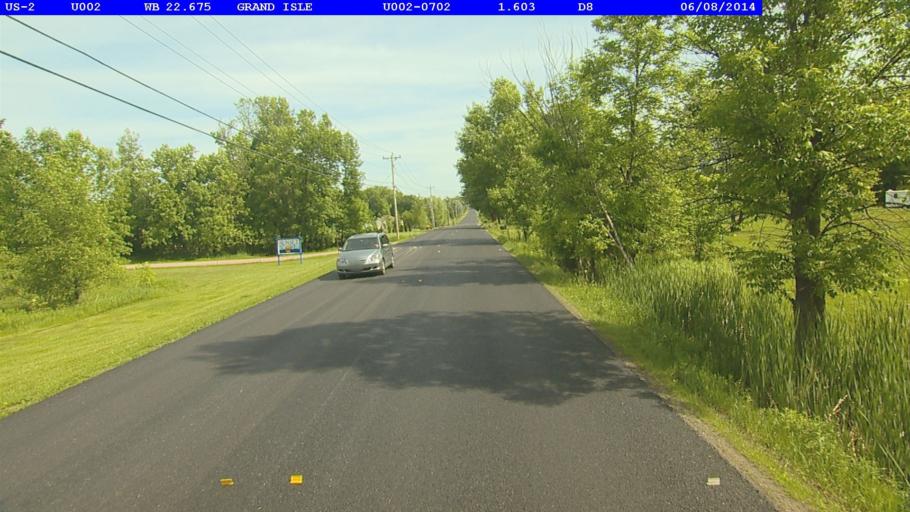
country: US
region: Vermont
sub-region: Grand Isle County
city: North Hero
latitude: 44.7443
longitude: -73.2888
